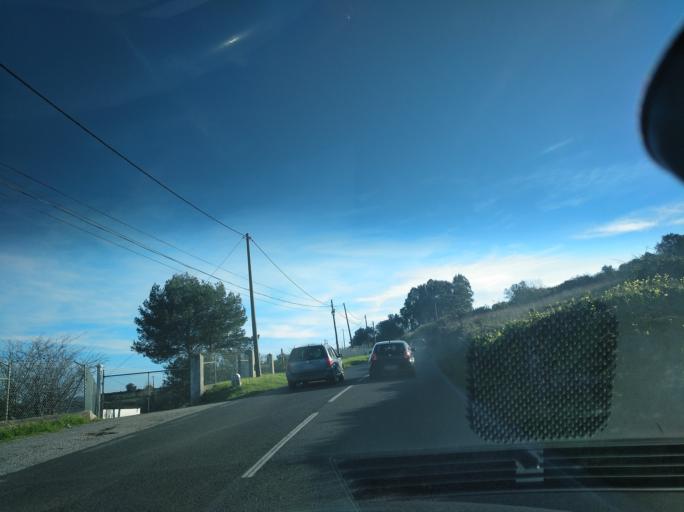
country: PT
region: Lisbon
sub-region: Sintra
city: Pero Pinheiro
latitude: 38.8820
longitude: -9.3300
